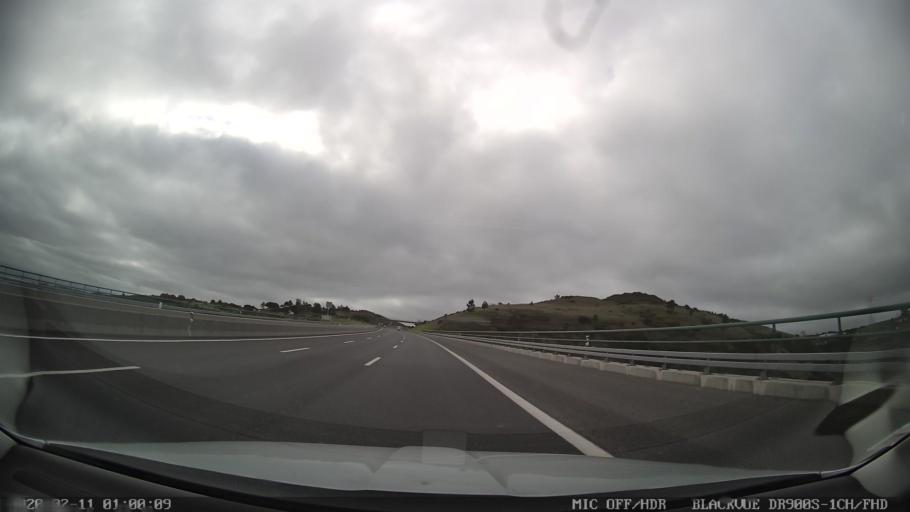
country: PT
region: Lisbon
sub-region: Vila Franca de Xira
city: Sobralinho
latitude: 38.9330
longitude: -9.0737
